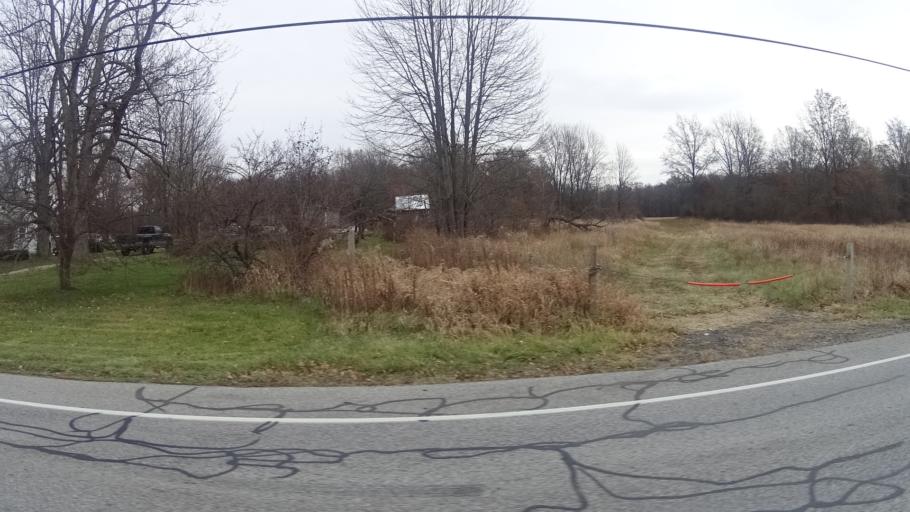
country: US
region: Ohio
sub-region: Cuyahoga County
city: Olmsted Falls
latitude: 41.3335
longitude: -81.9433
